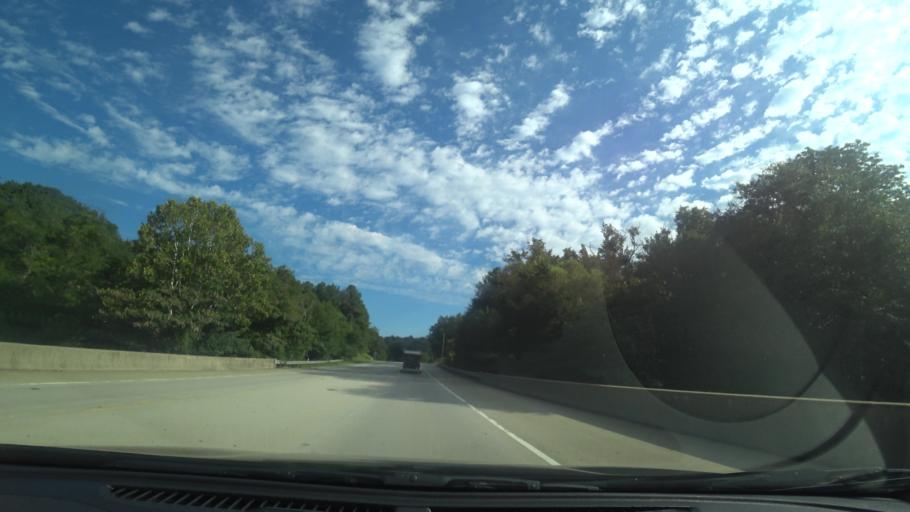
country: US
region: Georgia
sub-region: Rockdale County
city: Conyers
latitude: 33.6924
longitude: -83.9968
